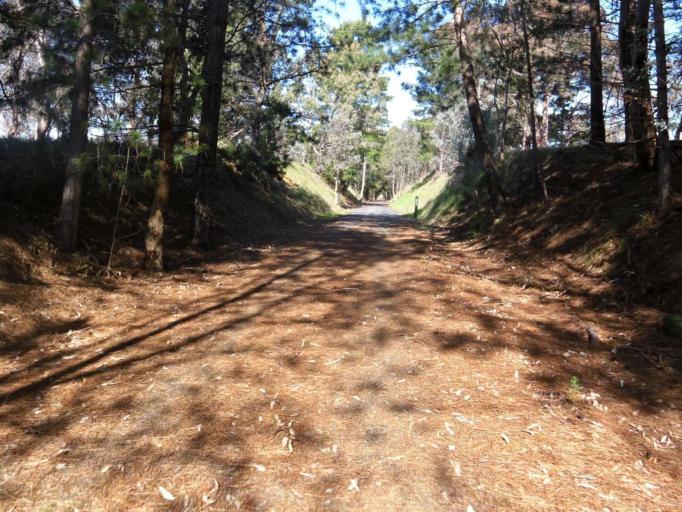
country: AU
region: Victoria
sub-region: Murrindindi
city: Alexandra
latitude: -36.9976
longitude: 145.7429
